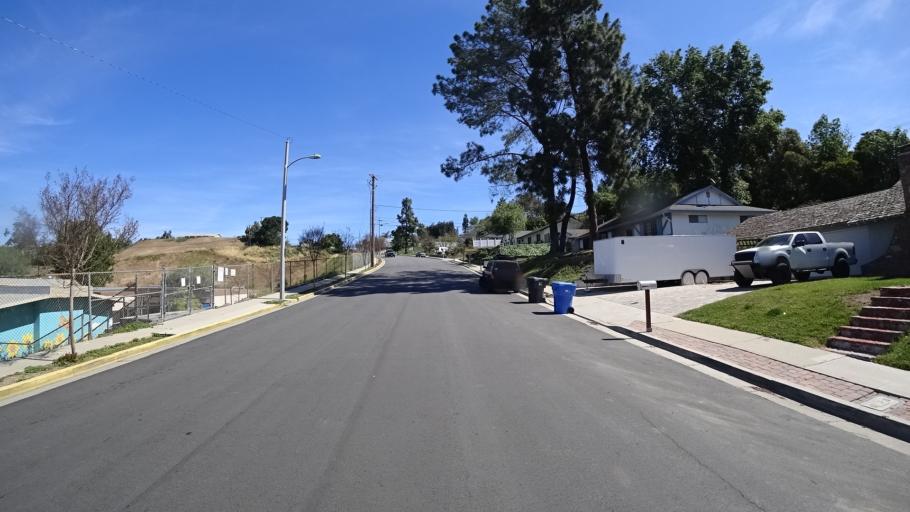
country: US
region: California
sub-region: Ventura County
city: Thousand Oaks
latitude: 34.2250
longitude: -118.8651
